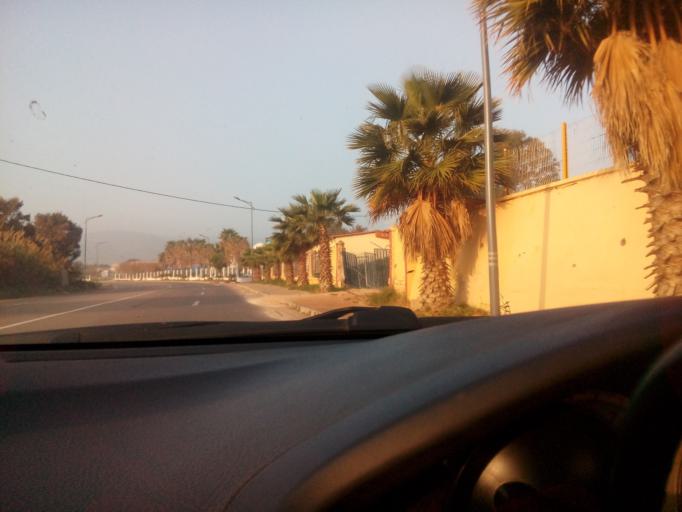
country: DZ
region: Oran
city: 'Ain el Turk
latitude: 35.7092
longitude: -0.8759
